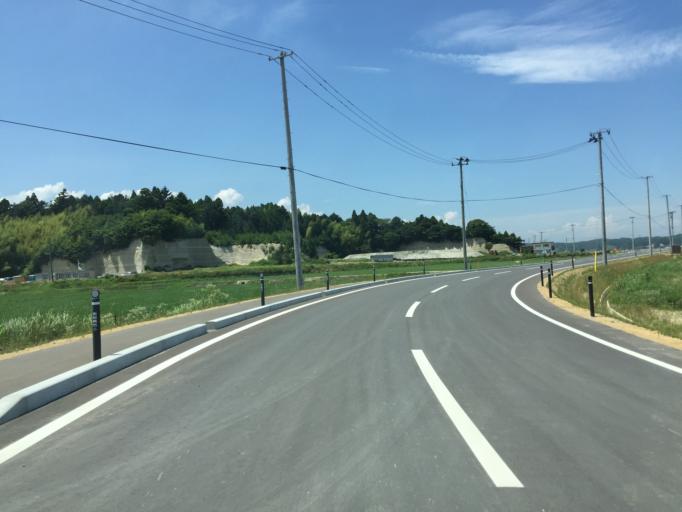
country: JP
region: Fukushima
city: Namie
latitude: 37.7197
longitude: 140.9984
